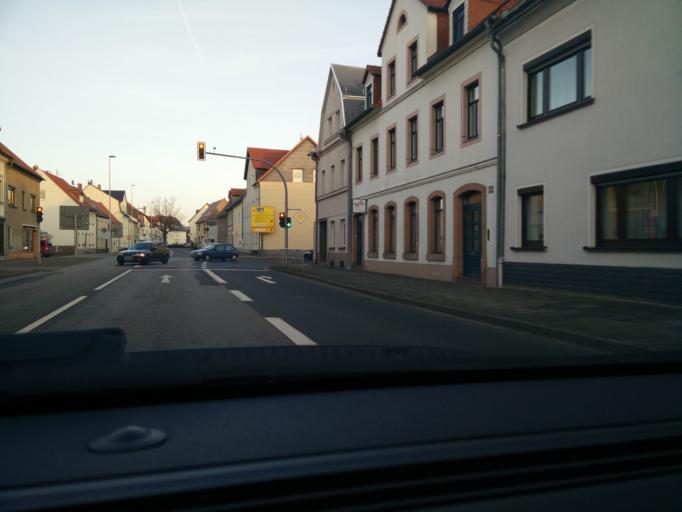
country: DE
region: Saxony
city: Bad Lausick
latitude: 51.1440
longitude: 12.6357
